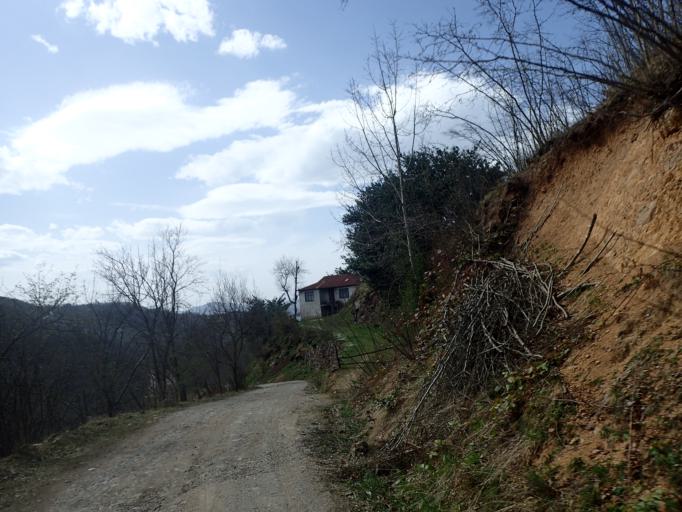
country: TR
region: Ordu
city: Kabaduz
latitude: 40.8145
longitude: 37.9030
